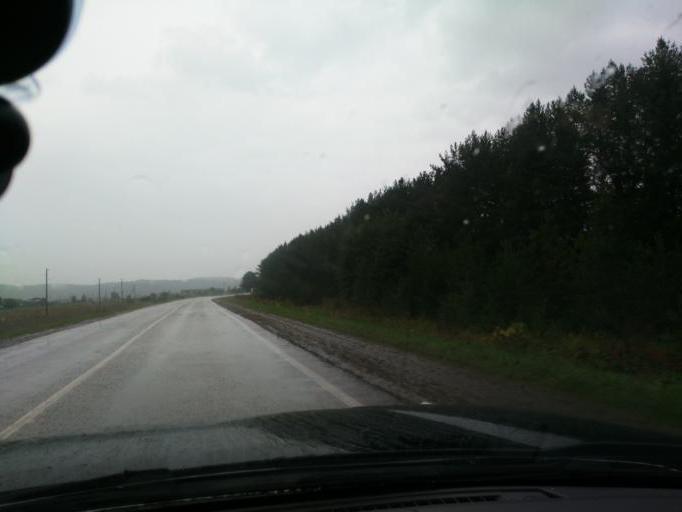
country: RU
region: Perm
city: Osa
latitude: 57.2879
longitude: 55.5736
